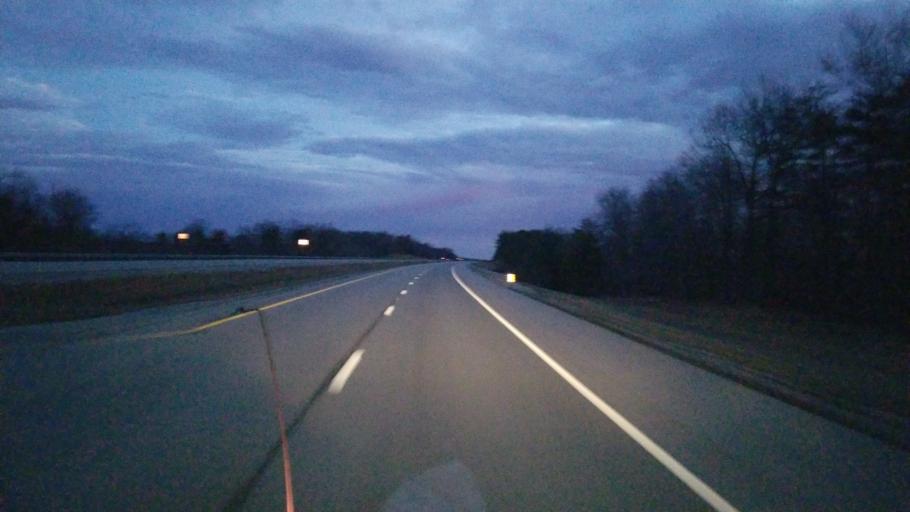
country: US
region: Tennessee
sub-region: Van Buren County
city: Spencer
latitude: 35.5557
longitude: -85.4710
